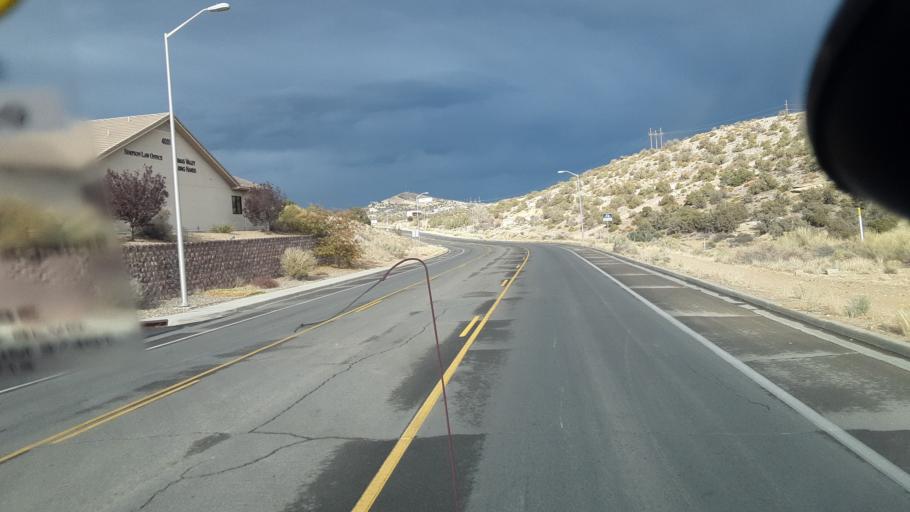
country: US
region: New Mexico
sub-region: San Juan County
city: Farmington
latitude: 36.7640
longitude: -108.1880
